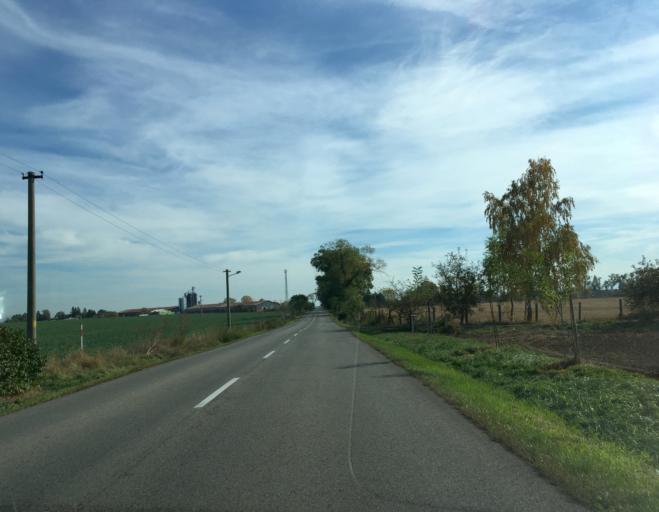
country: SK
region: Nitriansky
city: Zeliezovce
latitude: 48.0979
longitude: 18.5528
